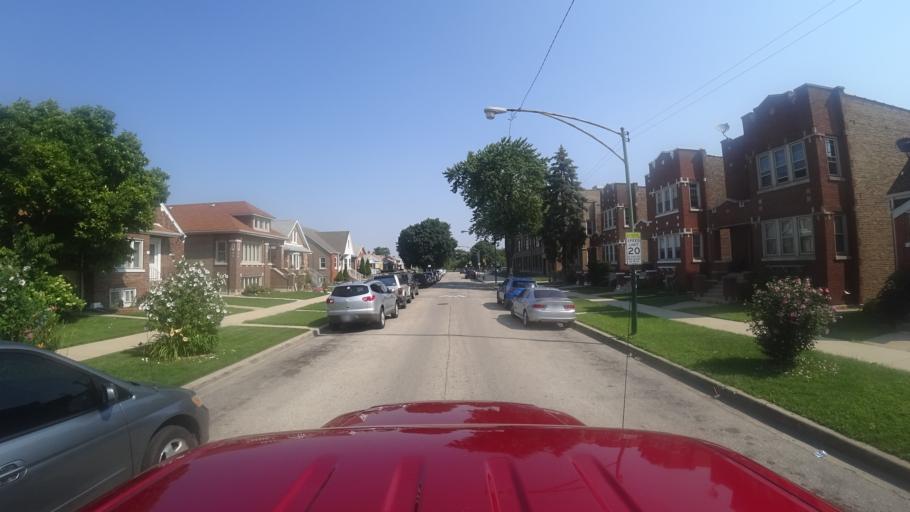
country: US
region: Illinois
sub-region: Cook County
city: Cicero
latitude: 41.8007
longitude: -87.7344
